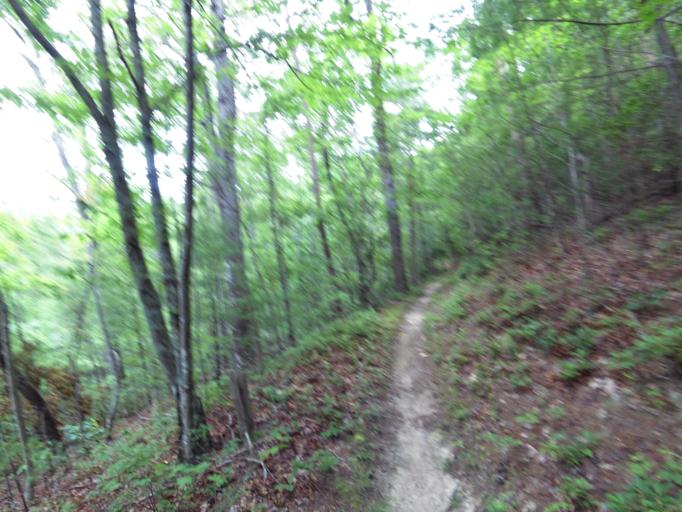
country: US
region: Tennessee
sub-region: Blount County
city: Wildwood
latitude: 35.6460
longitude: -83.8148
